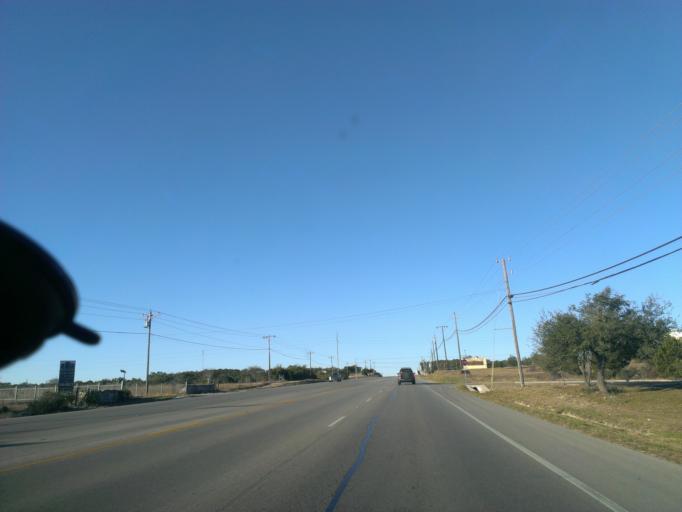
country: US
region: Texas
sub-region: Travis County
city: Bee Cave
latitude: 30.2262
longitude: -97.9466
